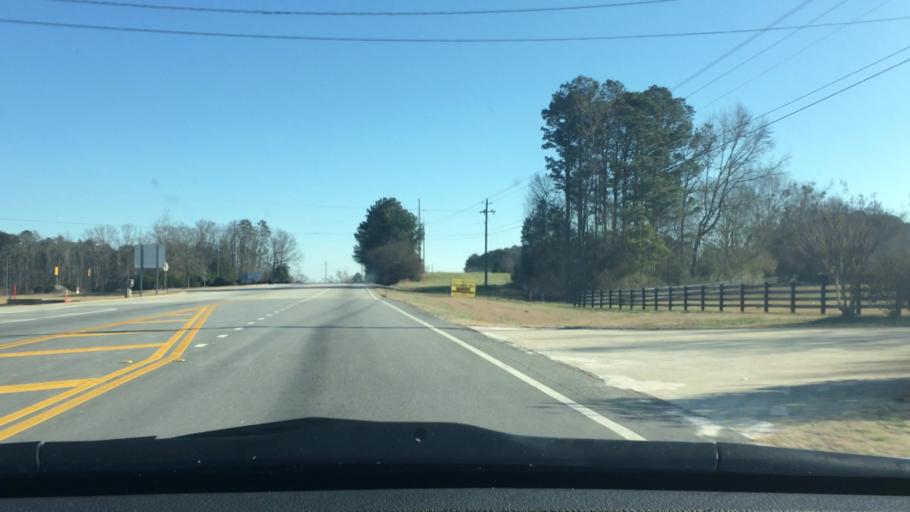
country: US
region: Georgia
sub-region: Henry County
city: McDonough
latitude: 33.5022
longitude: -84.0775
